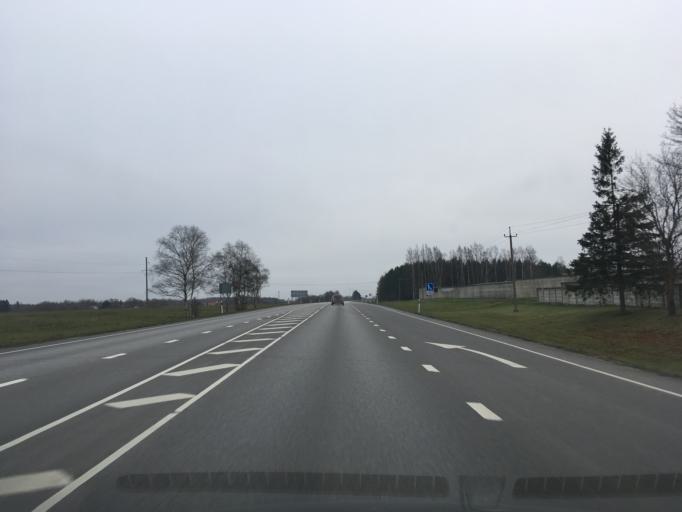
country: EE
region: Ida-Virumaa
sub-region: Kohtla-Jaerve linn
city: Kohtla-Jarve
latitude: 59.4102
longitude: 27.3113
